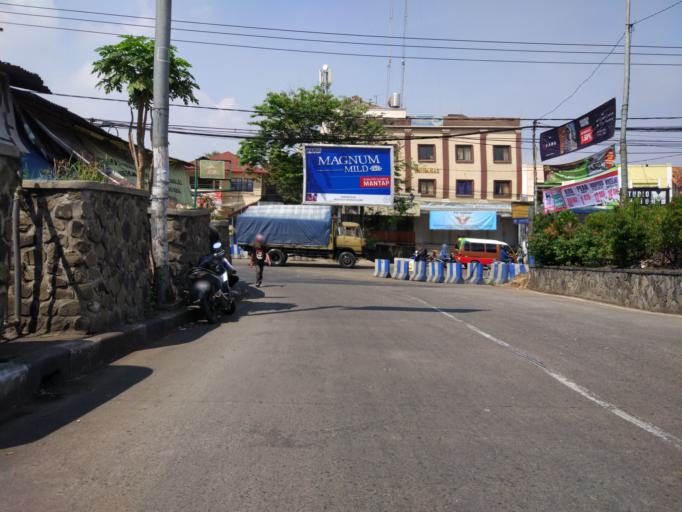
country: ID
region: West Java
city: Cileunyi
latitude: -6.9322
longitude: 107.7763
